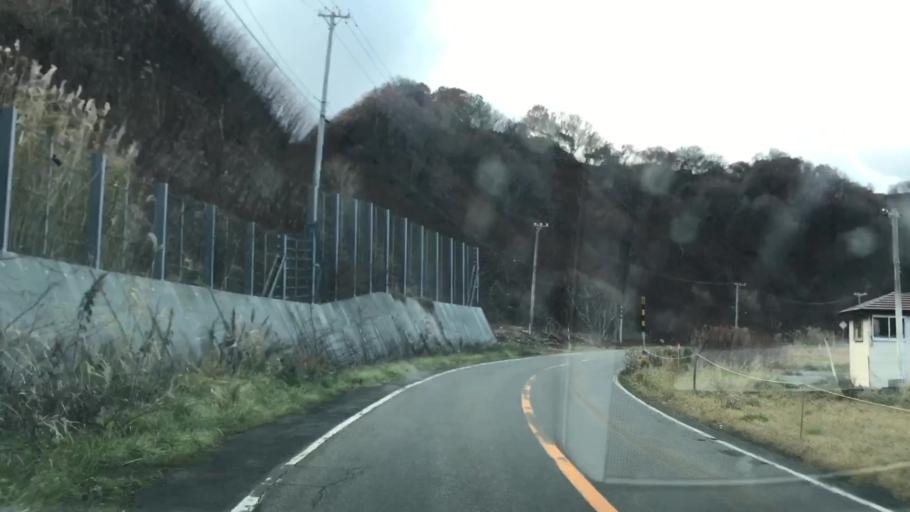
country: JP
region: Hokkaido
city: Yoichi
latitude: 43.3391
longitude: 140.4533
